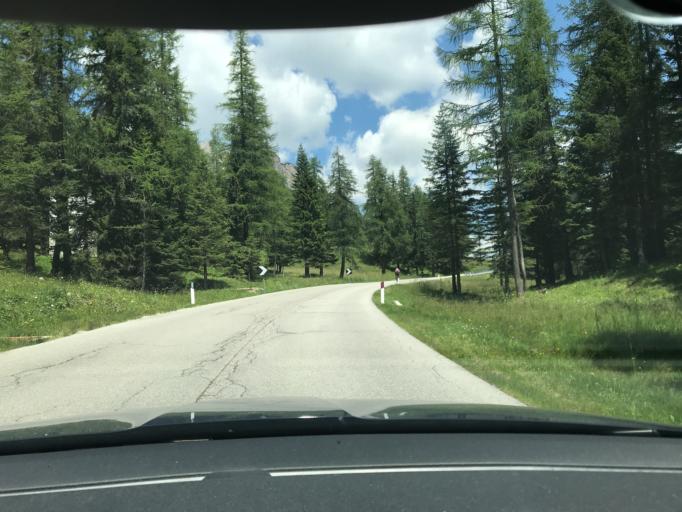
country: IT
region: Veneto
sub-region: Provincia di Belluno
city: Cortina d'Ampezzo
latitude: 46.5696
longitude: 12.2456
